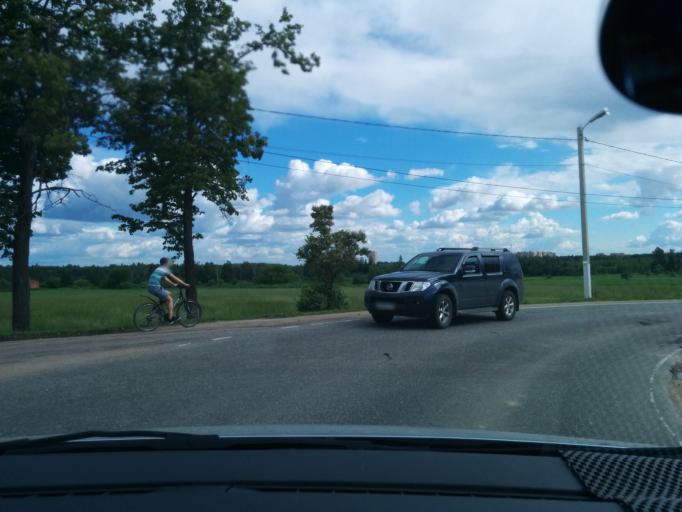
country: RU
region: Moskovskaya
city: Lugovaya
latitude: 56.0423
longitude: 37.4787
